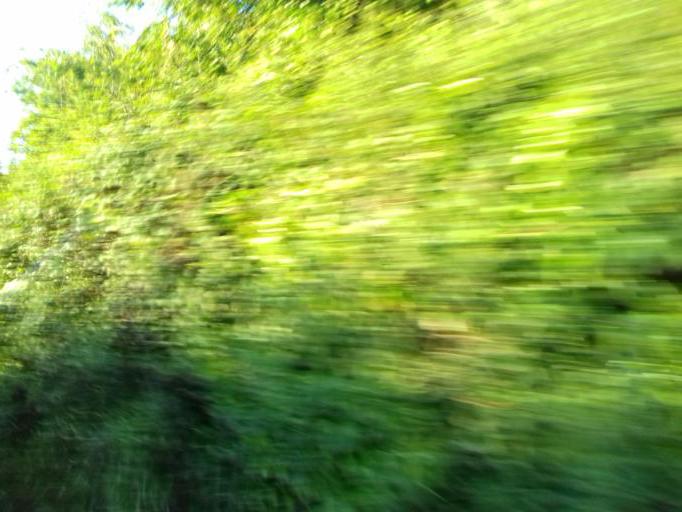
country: IE
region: Leinster
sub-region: An Mhi
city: Ashbourne
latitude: 53.5057
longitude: -6.3449
